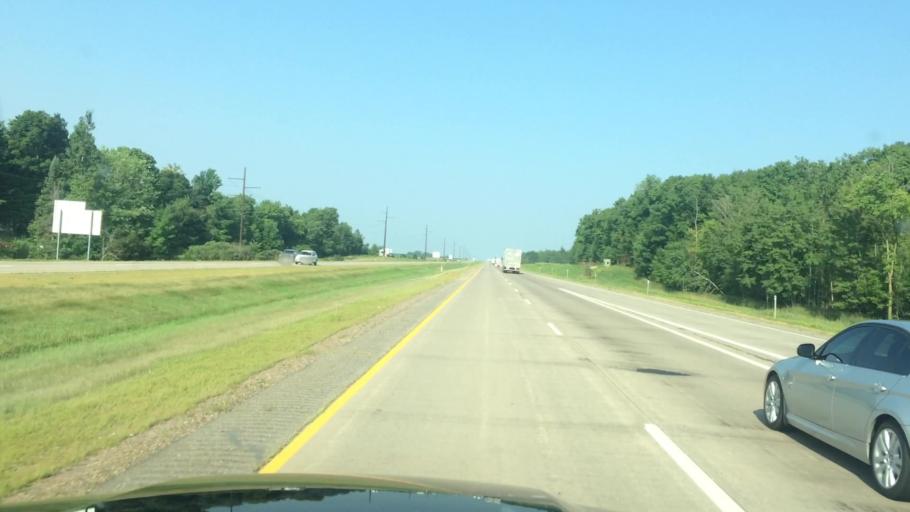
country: US
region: Wisconsin
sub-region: Marathon County
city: Edgar
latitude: 44.9445
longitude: -89.9687
